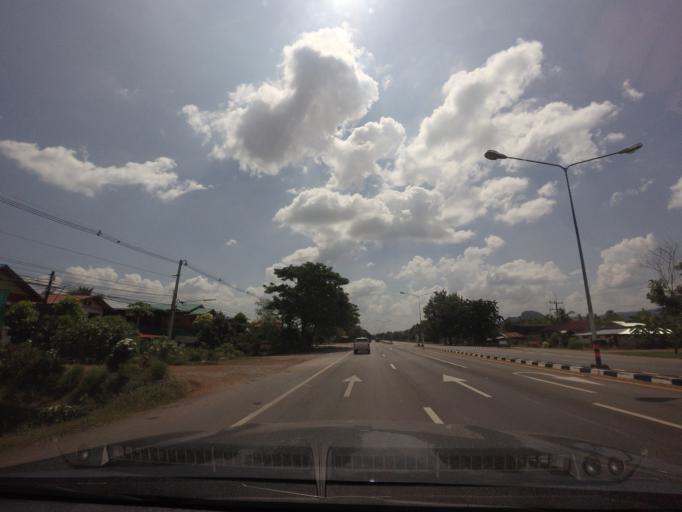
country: TH
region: Phetchabun
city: Nong Phai
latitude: 16.1339
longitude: 101.0471
